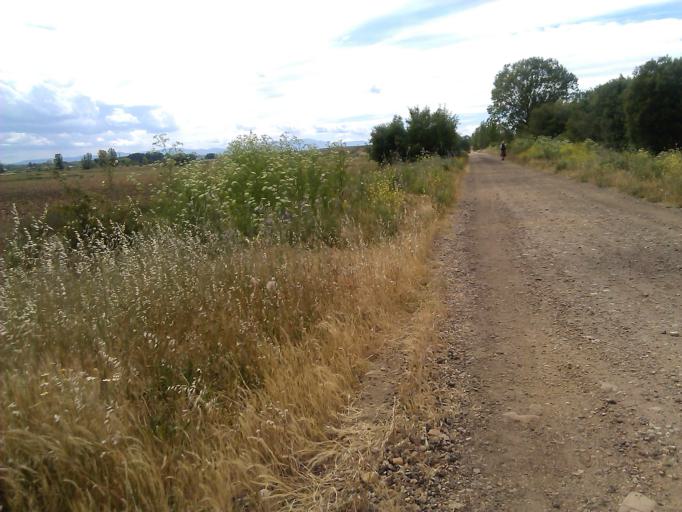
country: ES
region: Castille and Leon
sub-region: Provincia de Leon
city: Hospital de Orbigo
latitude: 42.4593
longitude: -5.8555
